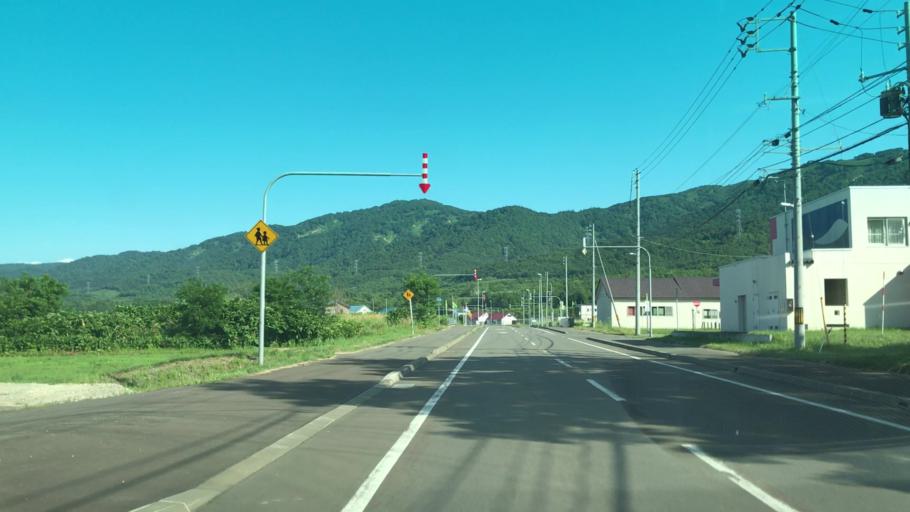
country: JP
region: Hokkaido
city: Yoichi
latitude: 43.0412
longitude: 140.7330
